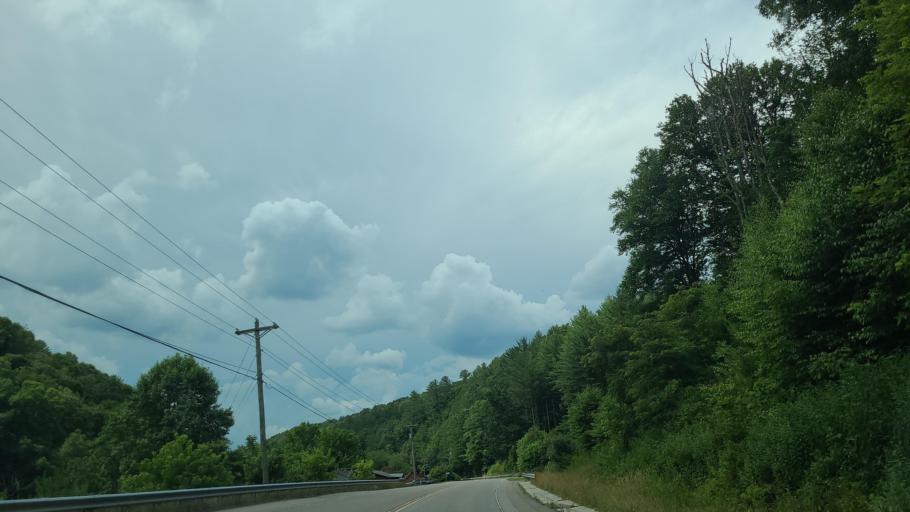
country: US
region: North Carolina
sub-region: Ashe County
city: Jefferson
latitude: 36.3816
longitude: -81.4004
